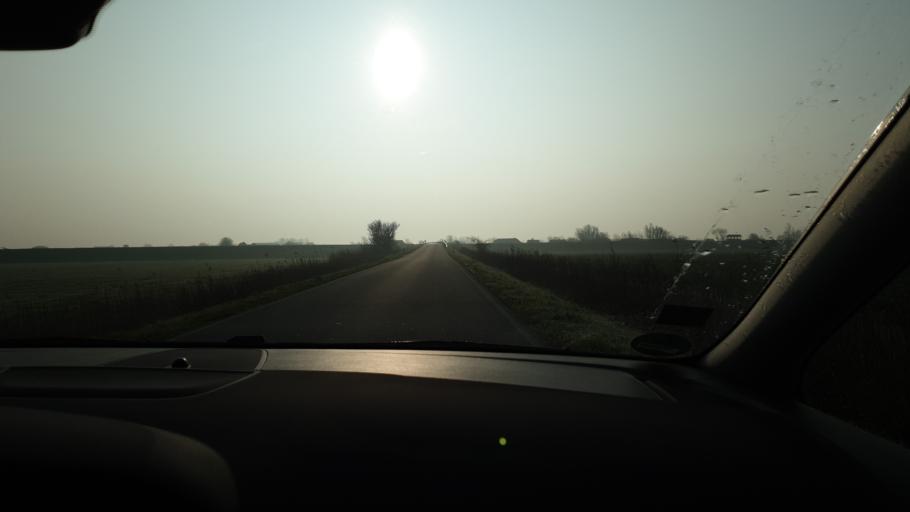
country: DE
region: Schleswig-Holstein
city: Elisabeth-Sophien-Koog
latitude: 54.4968
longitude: 8.9077
